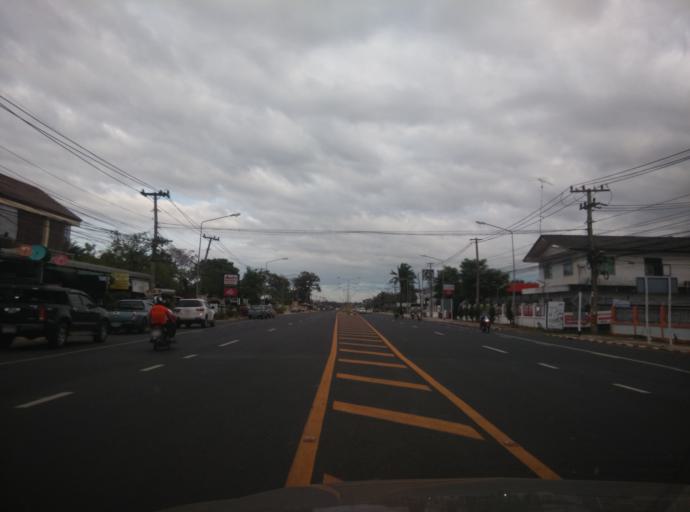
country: TH
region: Sisaket
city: Si Sa Ket
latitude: 15.1102
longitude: 104.3590
